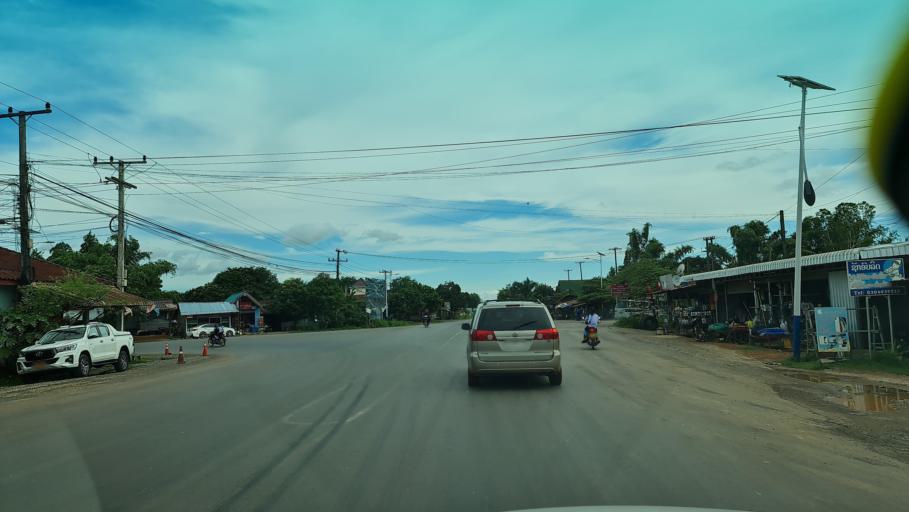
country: TH
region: Nakhon Phanom
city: Ban Phaeng
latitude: 18.0983
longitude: 104.2868
